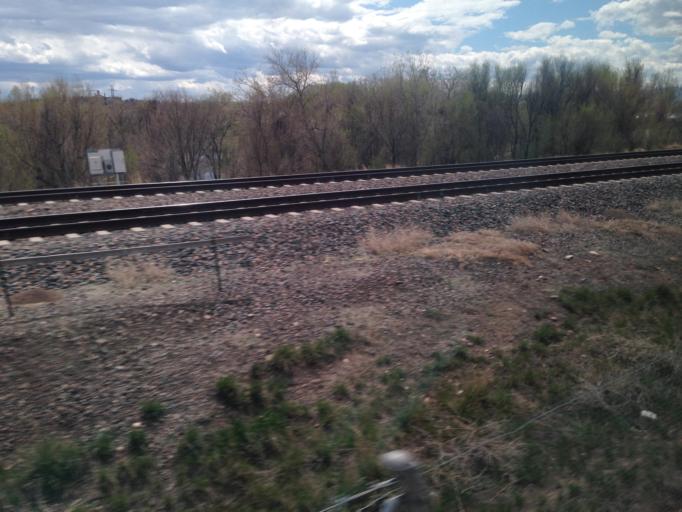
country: US
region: Colorado
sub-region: Adams County
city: Berkley
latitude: 39.8041
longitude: -105.0283
